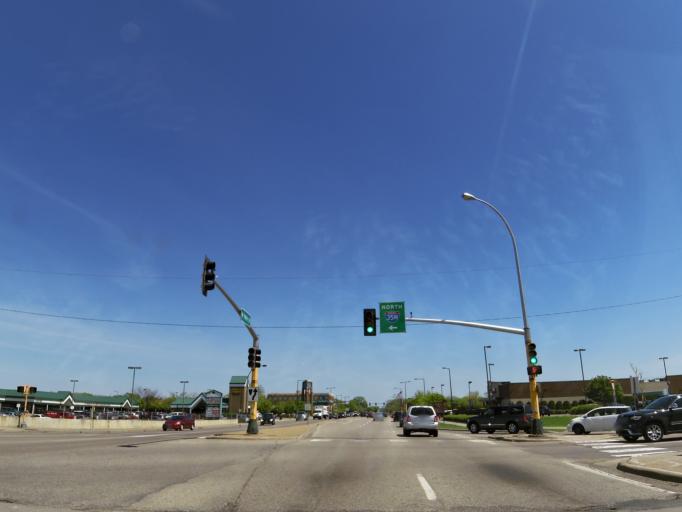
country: US
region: Minnesota
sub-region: Hennepin County
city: Bloomington
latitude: 44.8263
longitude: -93.2913
